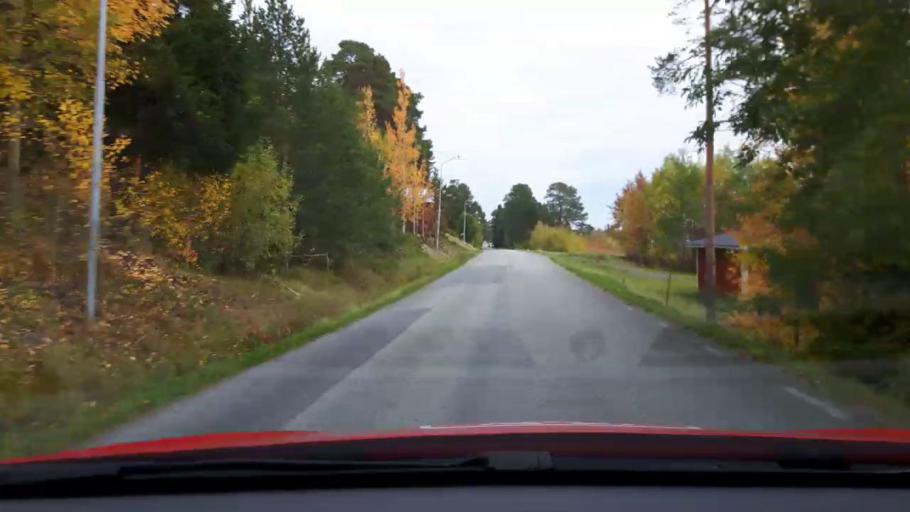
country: SE
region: Jaemtland
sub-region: Krokoms Kommun
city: Valla
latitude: 63.2574
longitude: 14.0180
